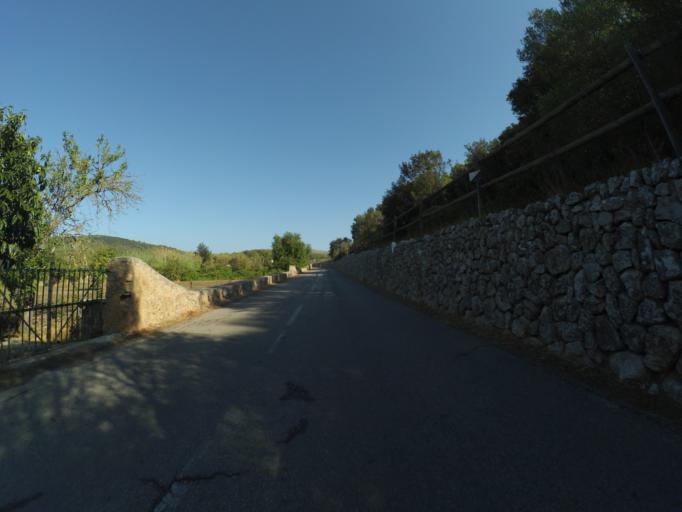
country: ES
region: Balearic Islands
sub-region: Illes Balears
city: Arta
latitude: 39.7039
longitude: 3.3513
